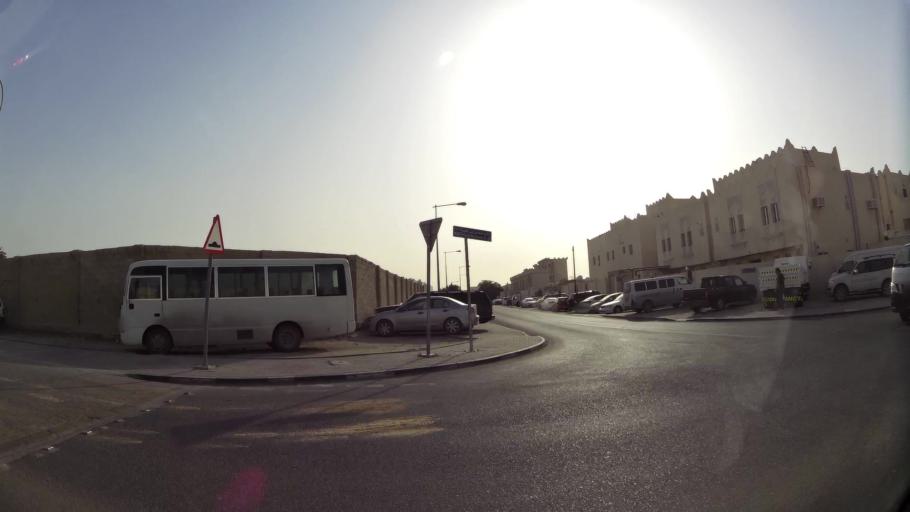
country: QA
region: Baladiyat ar Rayyan
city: Ar Rayyan
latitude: 25.2383
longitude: 51.4421
